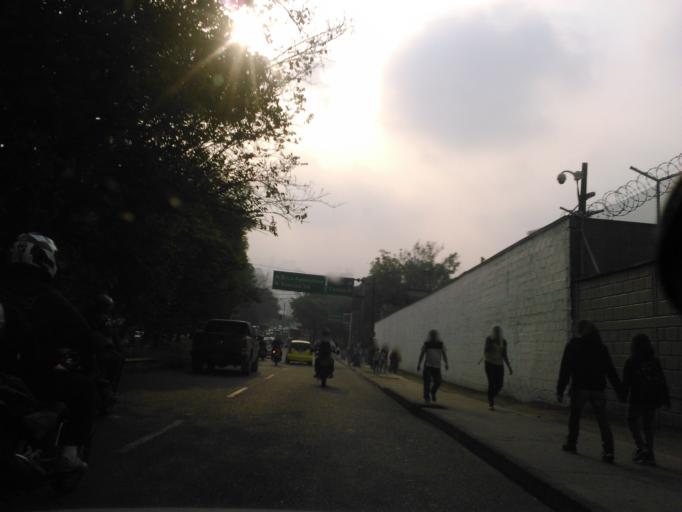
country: CO
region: Antioquia
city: Itagui
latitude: 6.1960
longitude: -75.5846
